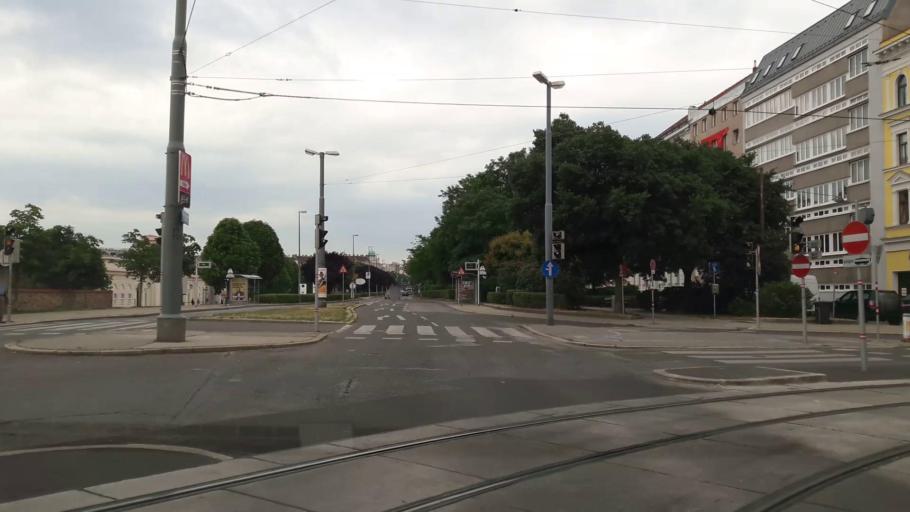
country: AT
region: Vienna
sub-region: Wien Stadt
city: Vienna
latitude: 48.2229
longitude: 16.3753
